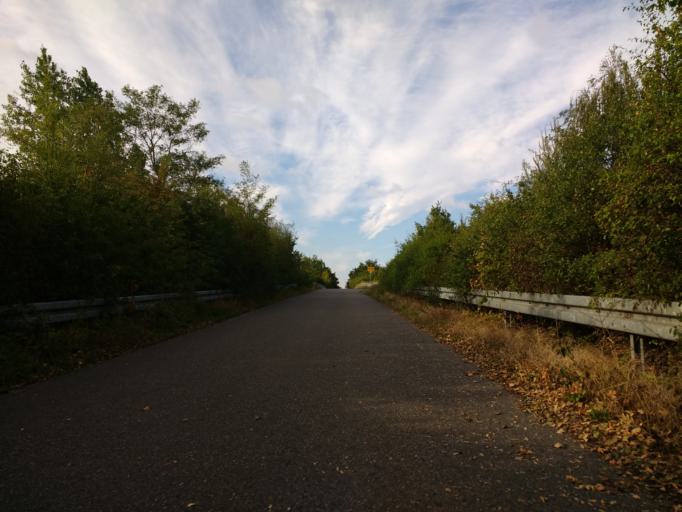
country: DE
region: Lower Saxony
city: Osloss
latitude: 52.4228
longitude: 10.6868
